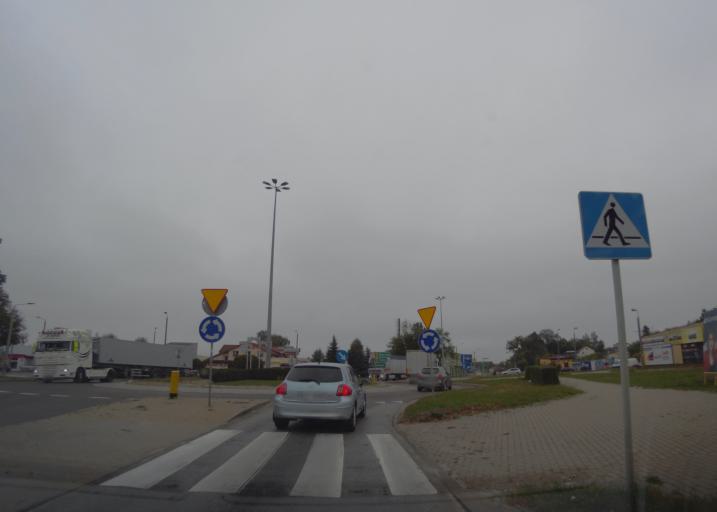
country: PL
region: Lublin Voivodeship
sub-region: Powiat krasnostawski
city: Krasnystaw
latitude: 50.9851
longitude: 23.1819
